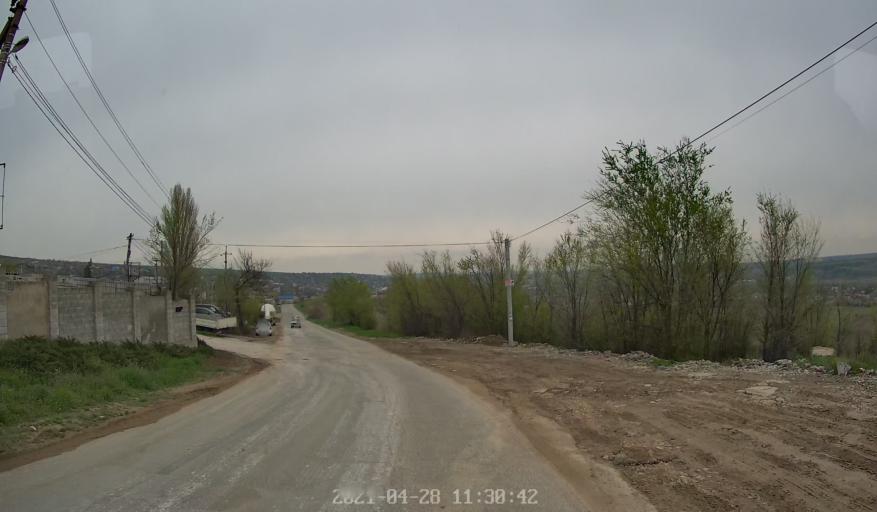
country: MD
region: Chisinau
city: Singera
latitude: 46.9734
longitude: 28.9366
